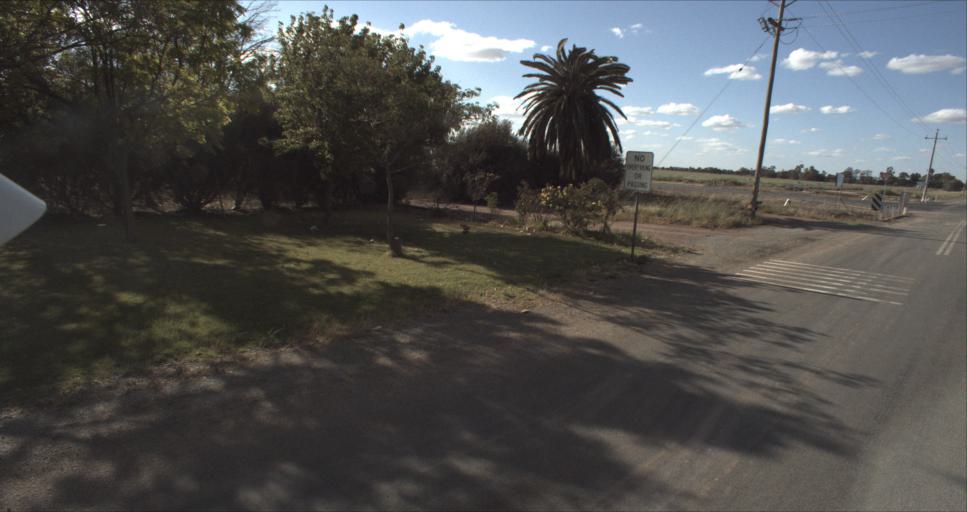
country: AU
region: New South Wales
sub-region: Leeton
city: Leeton
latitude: -34.5206
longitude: 146.2834
